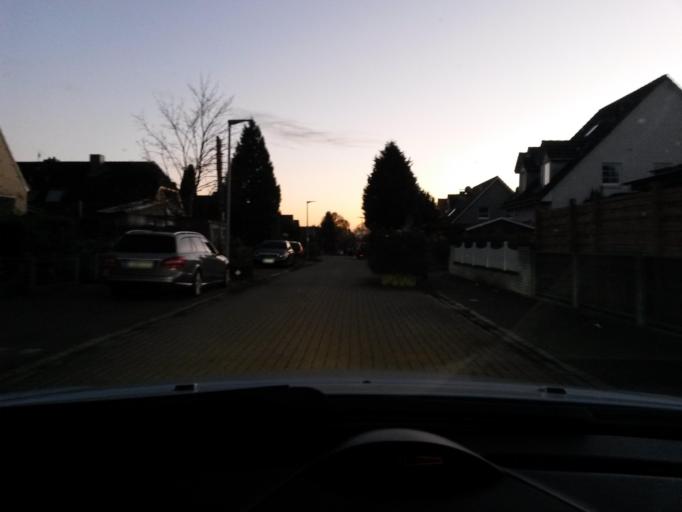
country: DE
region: Schleswig-Holstein
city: Barsbuettel
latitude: 53.5675
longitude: 10.1711
